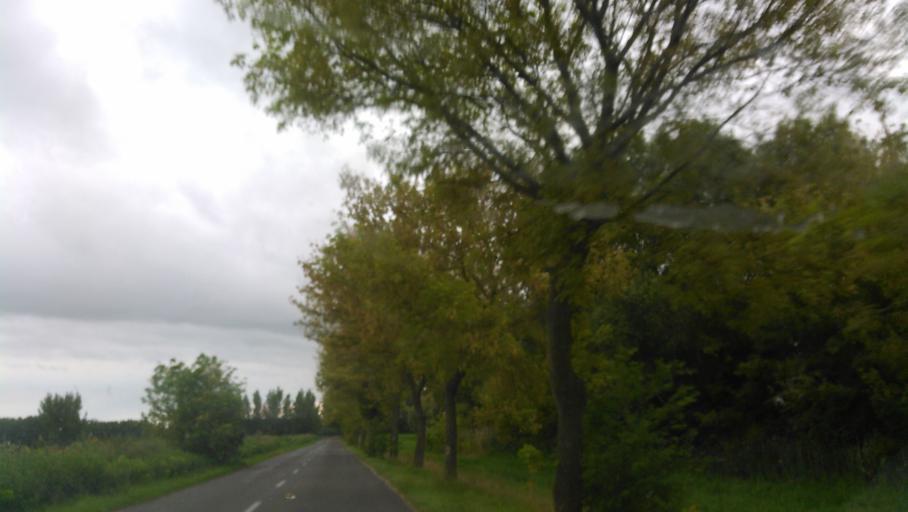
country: SK
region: Trnavsky
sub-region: Okres Dunajska Streda
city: Velky Meder
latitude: 47.9149
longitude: 17.7521
